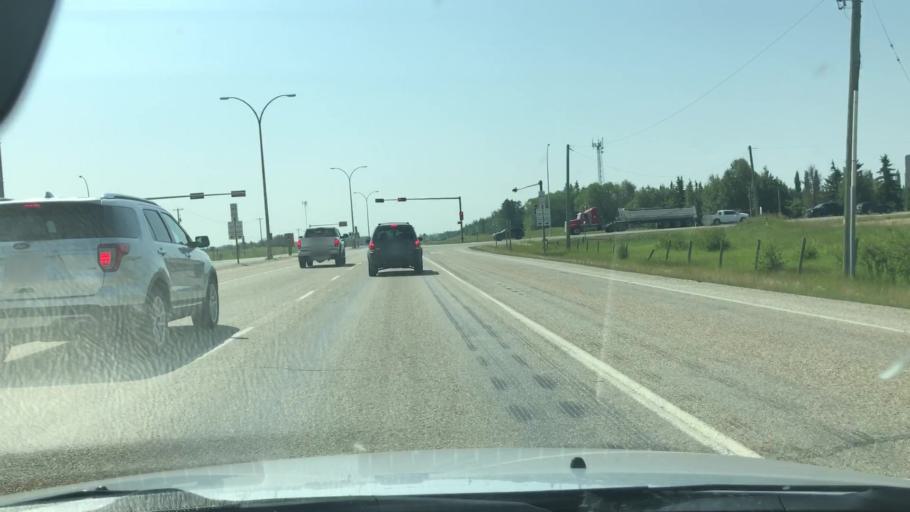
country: CA
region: Alberta
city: Devon
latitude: 53.4550
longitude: -113.7626
